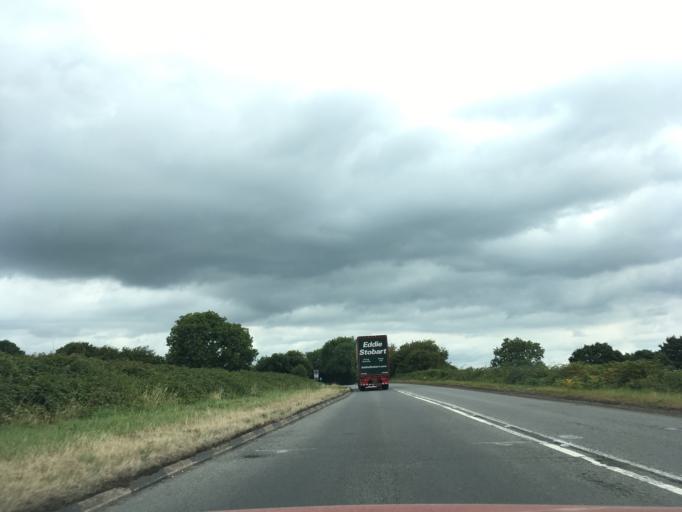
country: GB
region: Wales
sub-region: Torfaen County Borough
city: New Inn
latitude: 51.7262
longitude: -2.9881
